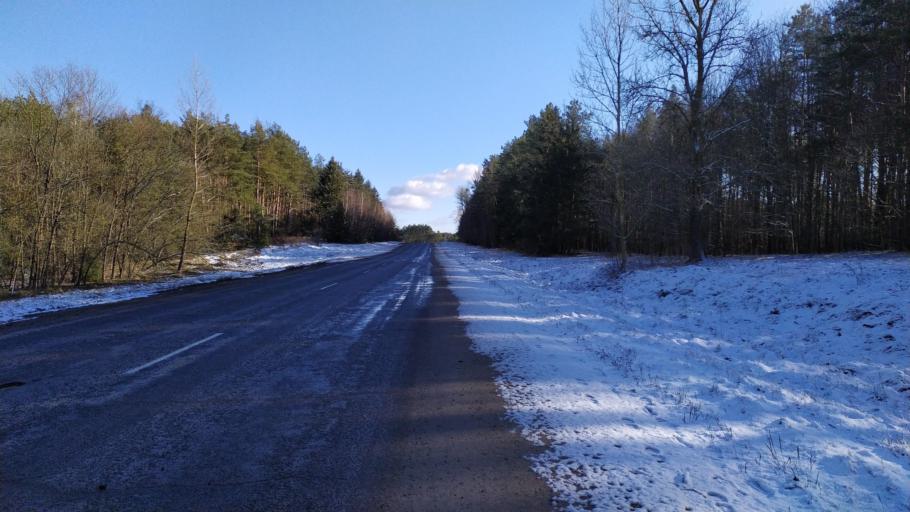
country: BY
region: Brest
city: Kamyanyets
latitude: 52.3890
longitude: 23.8429
